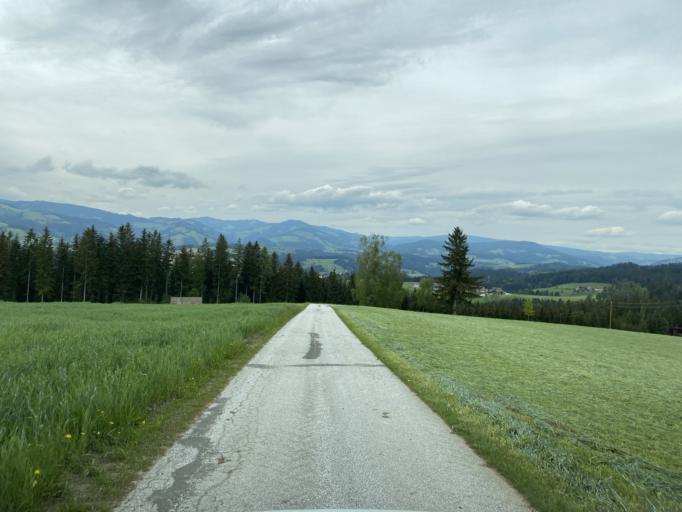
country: AT
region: Styria
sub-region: Politischer Bezirk Weiz
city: Gschaid bei Birkfeld
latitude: 47.3360
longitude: 15.7214
